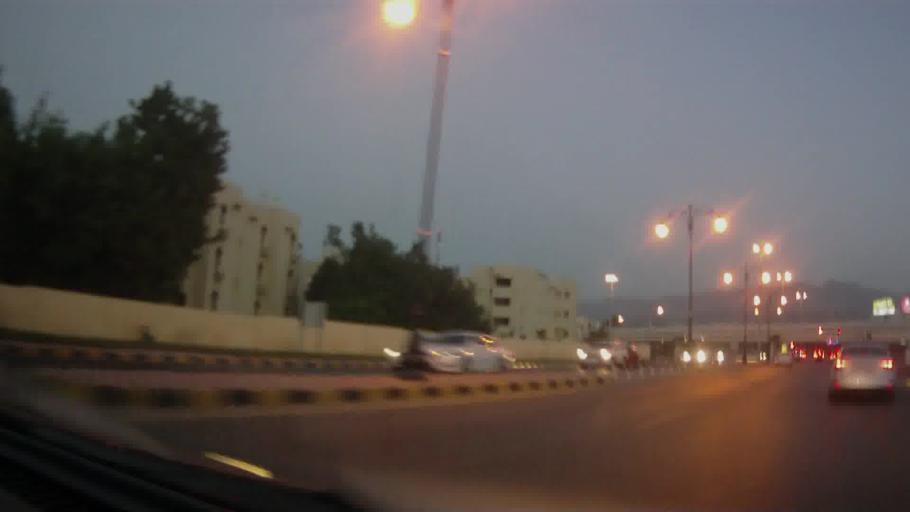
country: OM
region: Muhafazat Masqat
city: Bawshar
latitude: 23.5996
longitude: 58.4418
